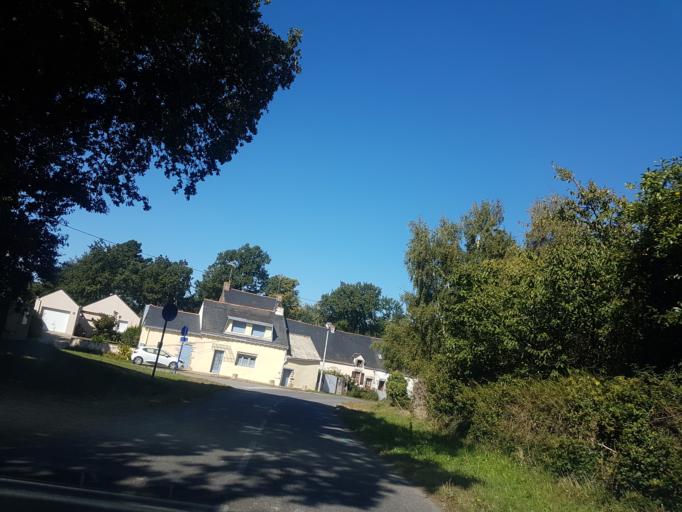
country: FR
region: Pays de la Loire
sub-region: Departement de la Loire-Atlantique
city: Mesquer
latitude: 47.3920
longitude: -2.4480
